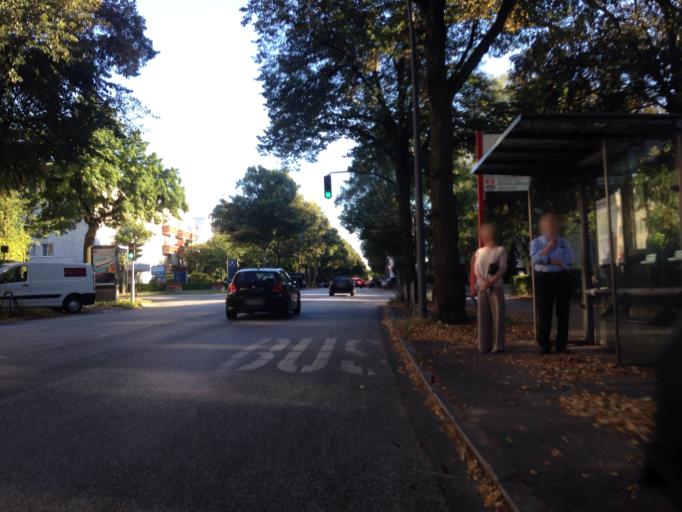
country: DE
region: Hamburg
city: Hamburg-Nord
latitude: 53.5782
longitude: 9.9890
